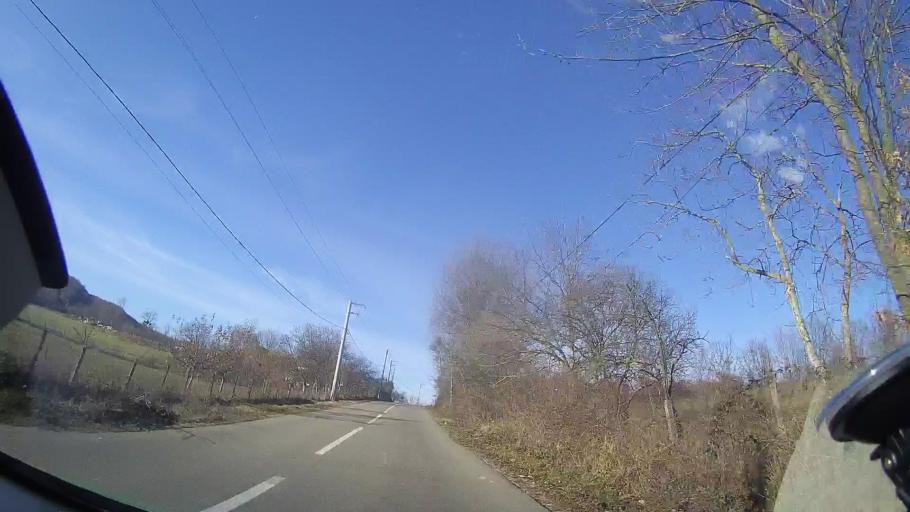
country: RO
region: Bihor
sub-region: Comuna Vadu Crisului
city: Vadu Crisului
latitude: 46.9735
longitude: 22.5409
